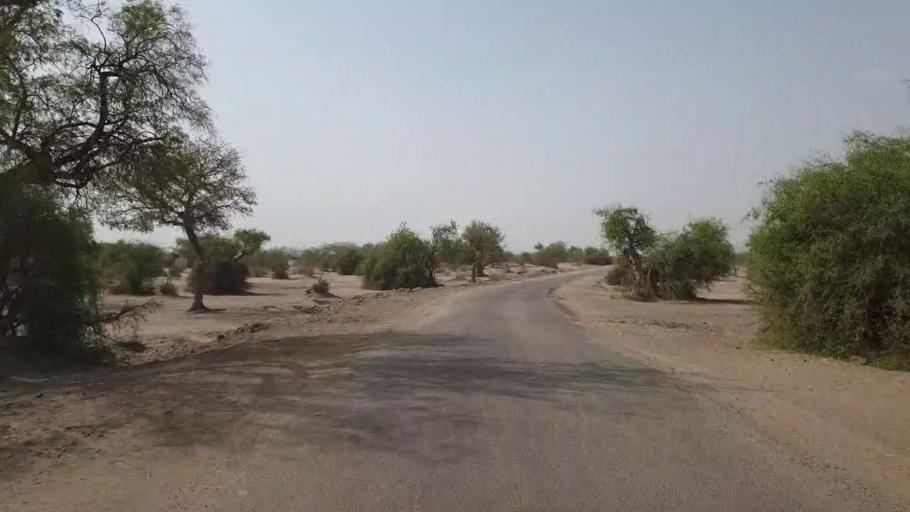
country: PK
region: Sindh
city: Mithi
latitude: 24.6089
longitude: 69.9206
